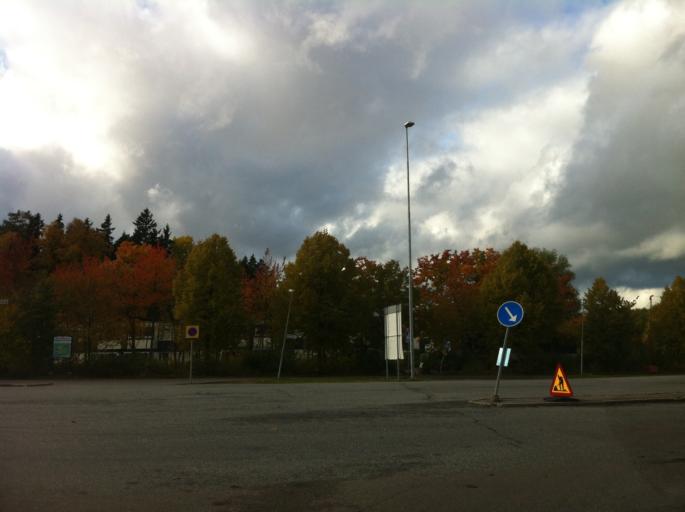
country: SE
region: Stockholm
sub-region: Upplands Vasby Kommun
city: Upplands Vaesby
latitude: 59.5133
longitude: 17.9194
